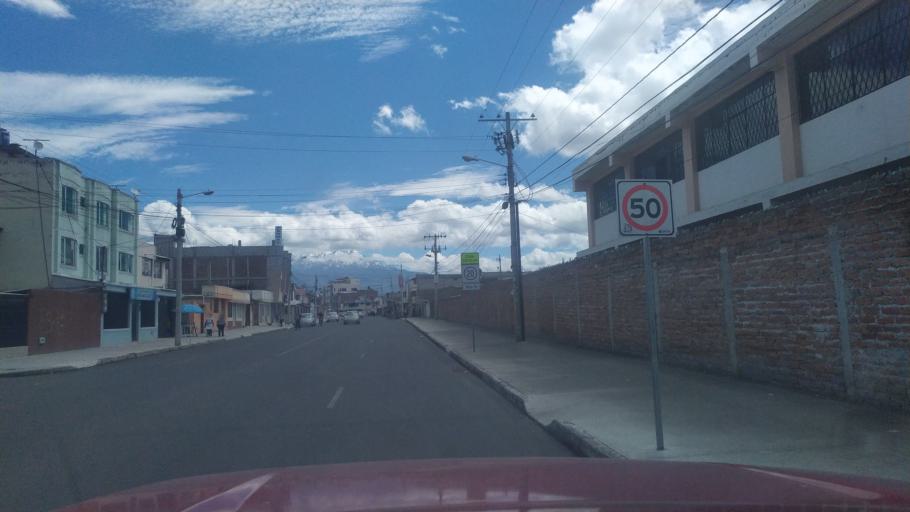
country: EC
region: Chimborazo
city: Riobamba
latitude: -1.6815
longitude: -78.6452
